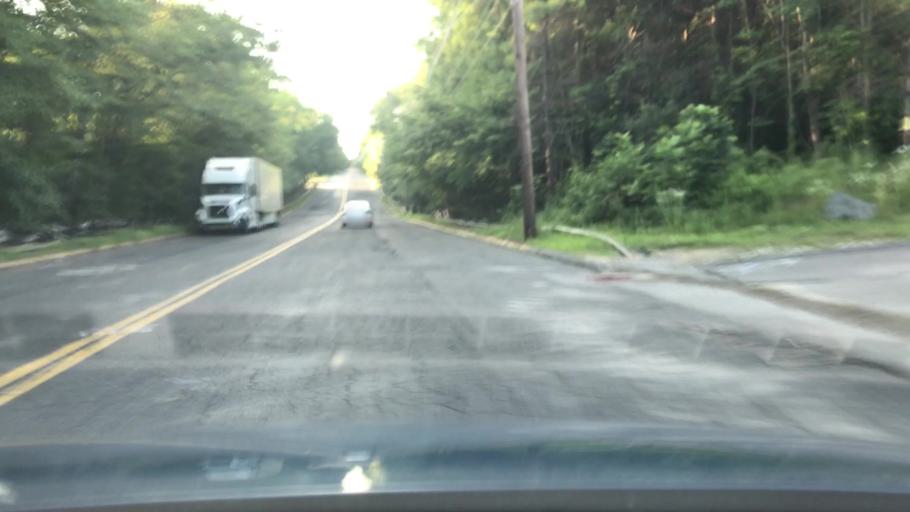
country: US
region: Massachusetts
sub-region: Worcester County
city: Northborough
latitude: 42.3258
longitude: -71.5983
